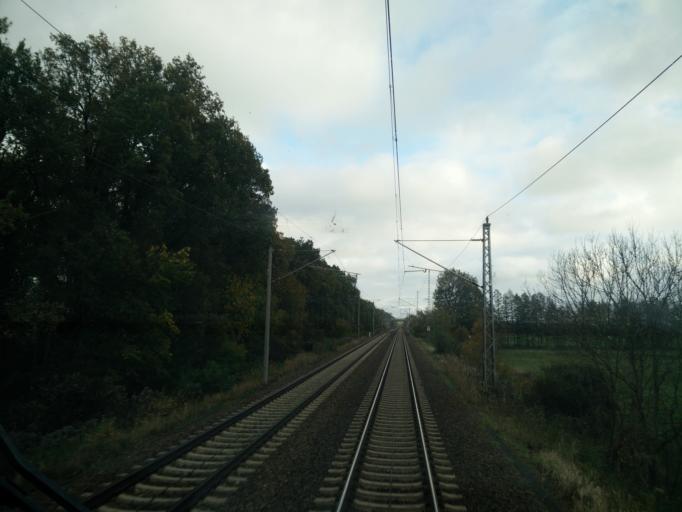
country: DE
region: Brandenburg
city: Wusterhausen
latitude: 52.8752
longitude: 12.4011
